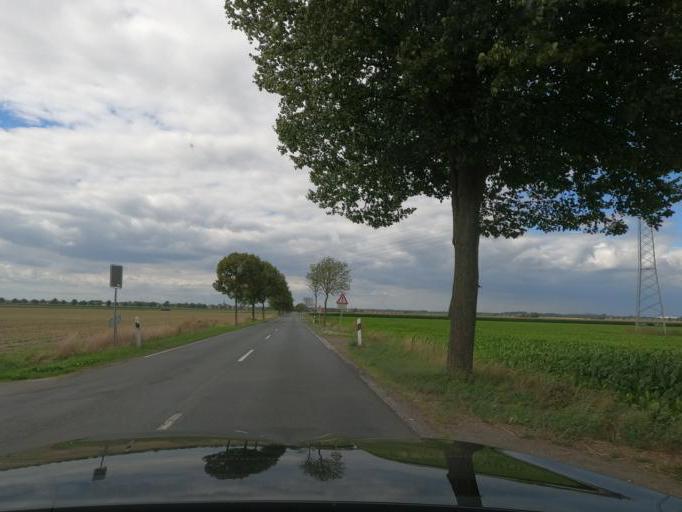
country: DE
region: Lower Saxony
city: Algermissen
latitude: 52.2453
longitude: 9.9997
